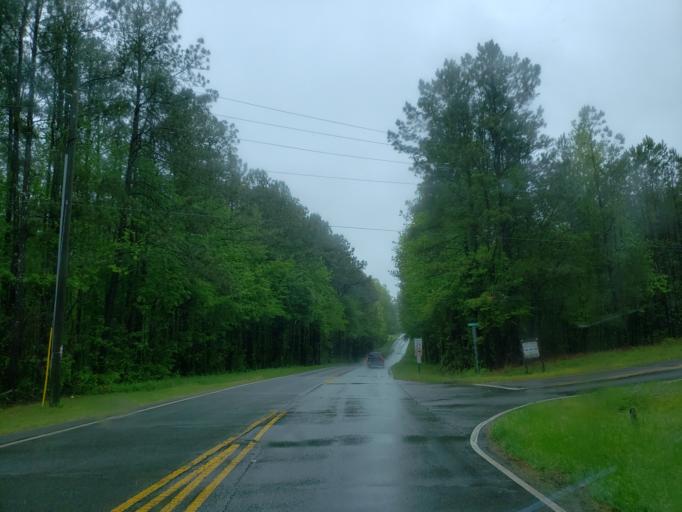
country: US
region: Georgia
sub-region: Haralson County
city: Bremen
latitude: 33.6921
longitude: -85.1884
